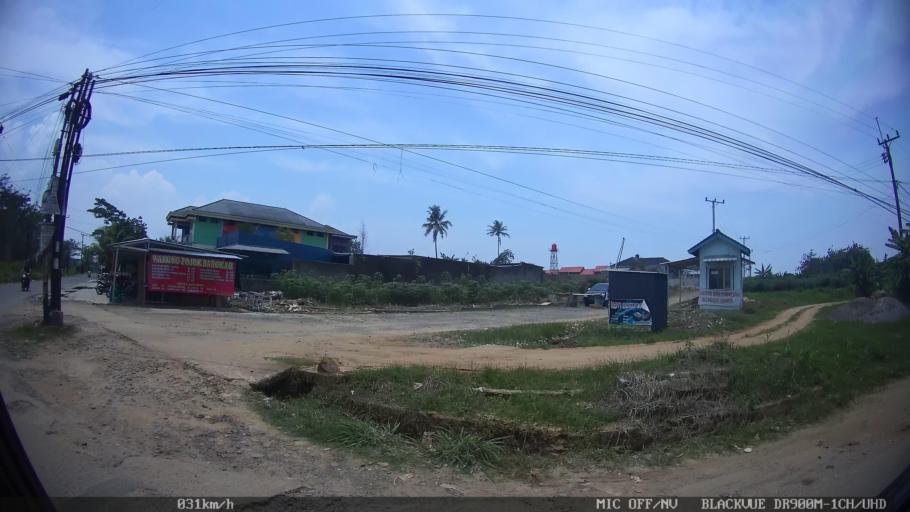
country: ID
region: Lampung
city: Kedaton
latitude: -5.3484
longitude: 105.2425
